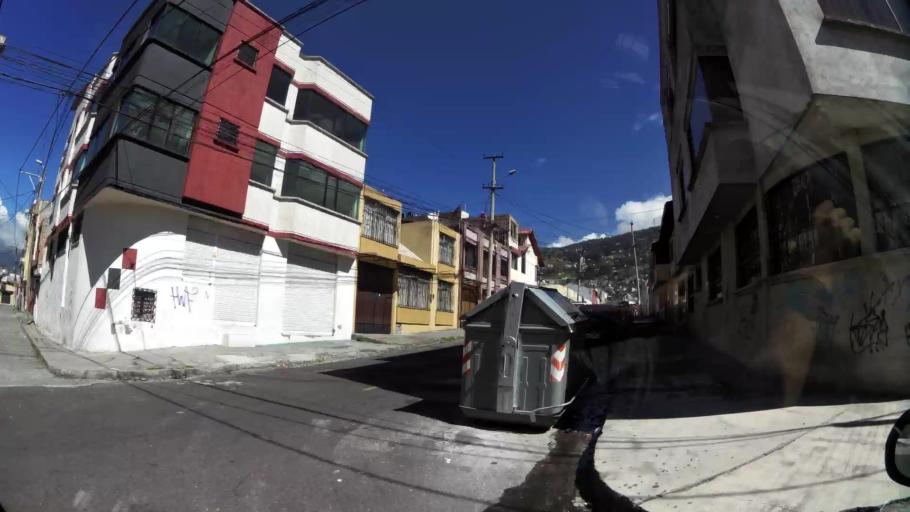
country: EC
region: Pichincha
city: Quito
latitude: -0.2391
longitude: -78.5285
